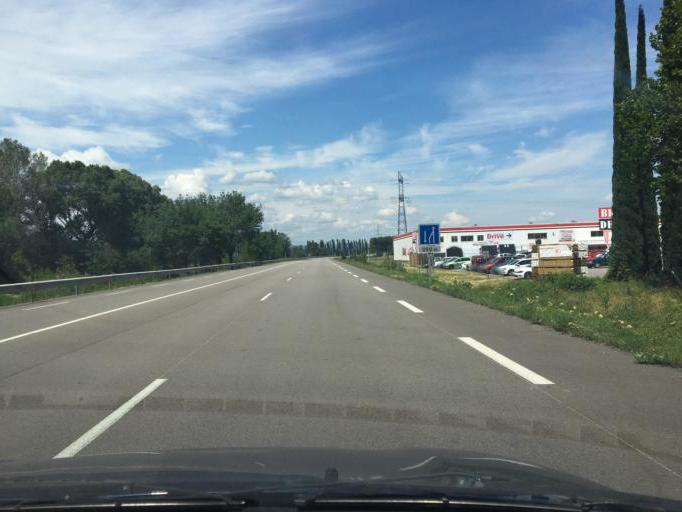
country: FR
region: Rhone-Alpes
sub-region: Departement de la Drome
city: Saulce-sur-Rhone
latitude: 44.6787
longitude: 4.7944
